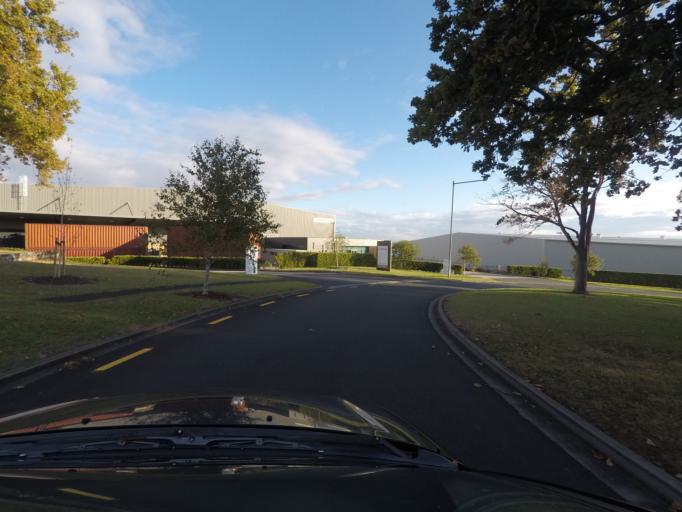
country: NZ
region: Auckland
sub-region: Auckland
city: Manukau City
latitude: -36.9421
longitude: 174.8692
